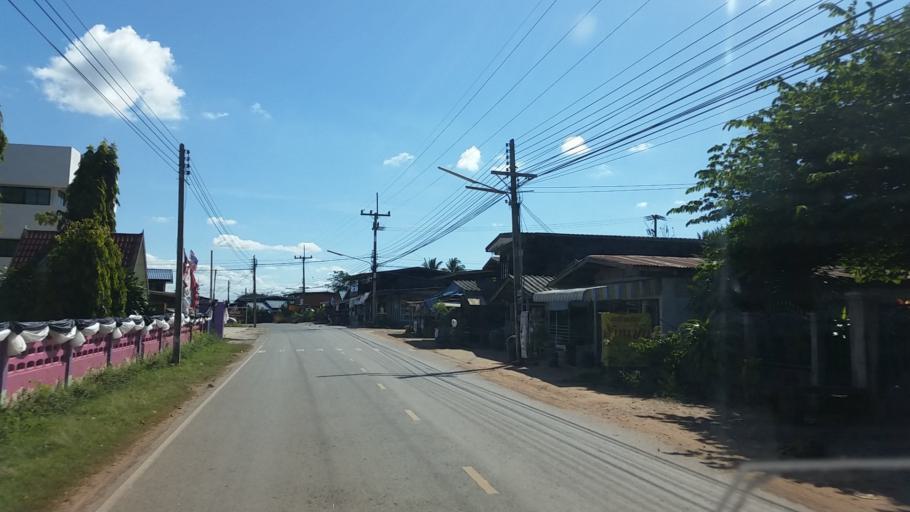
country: TH
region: Chaiyaphum
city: Thep Sathit
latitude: 15.5512
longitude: 101.4106
